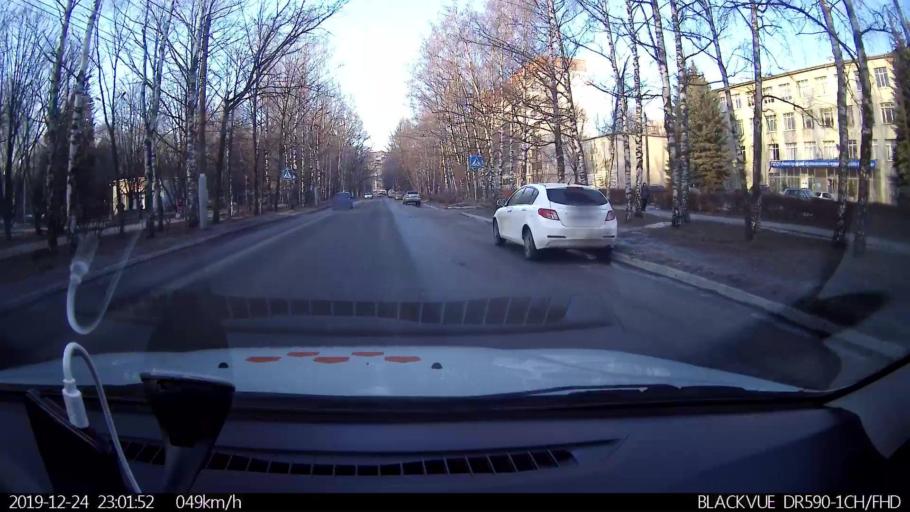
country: RU
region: Nizjnij Novgorod
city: Nizhniy Novgorod
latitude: 56.2690
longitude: 43.9236
